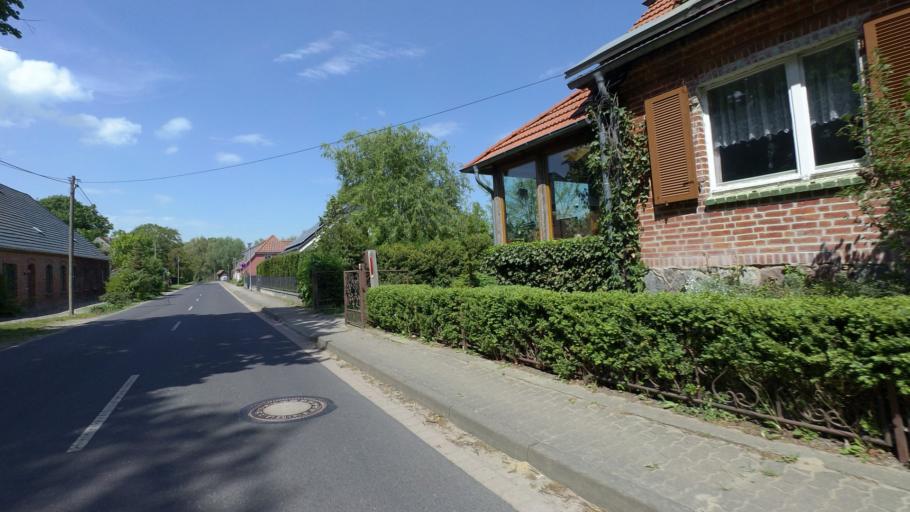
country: DE
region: Mecklenburg-Vorpommern
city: Mollenhagen
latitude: 53.5795
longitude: 12.8922
